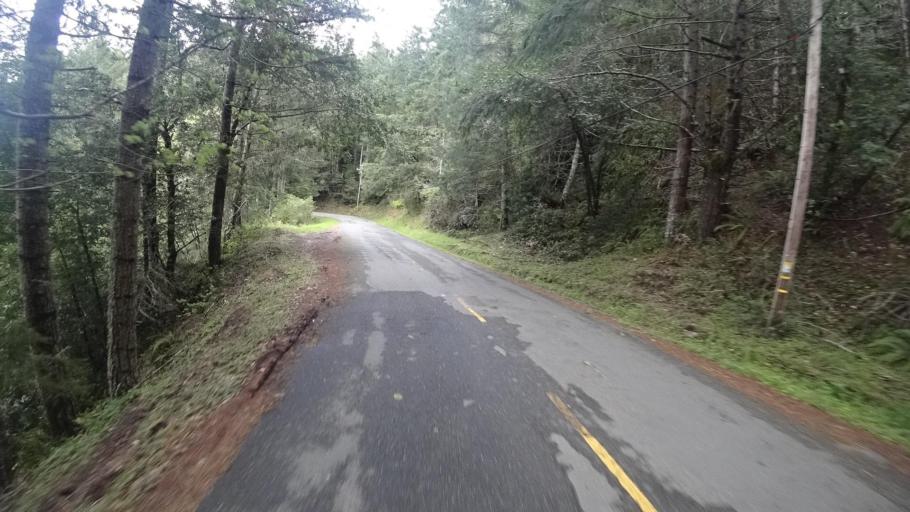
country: US
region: California
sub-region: Humboldt County
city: Bayside
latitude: 40.7511
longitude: -123.9720
